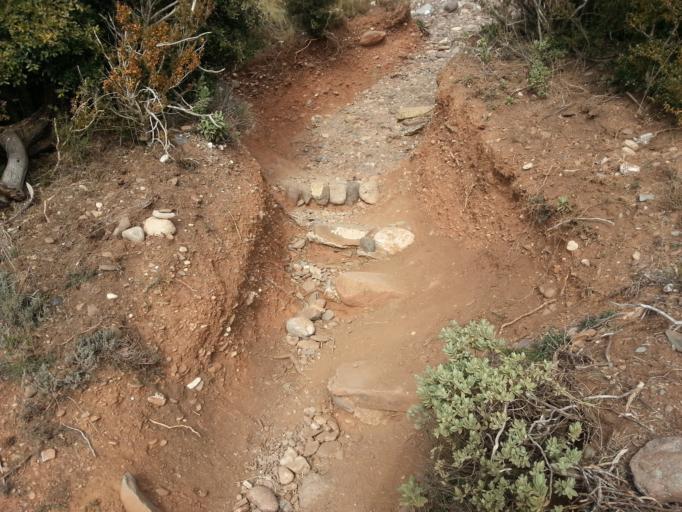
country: ES
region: Catalonia
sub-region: Provincia de Barcelona
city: Mura
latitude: 41.6744
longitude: 2.0046
